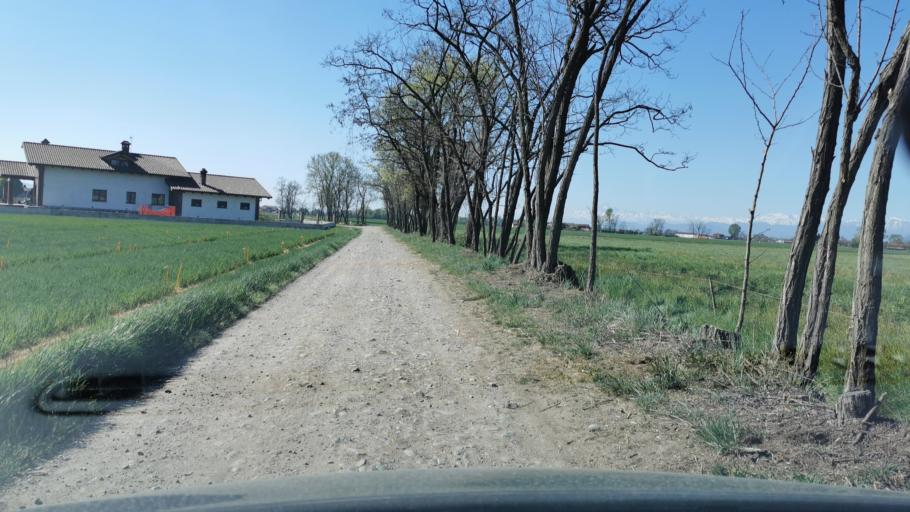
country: IT
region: Piedmont
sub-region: Provincia di Torino
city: Leini
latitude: 45.1998
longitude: 7.6851
